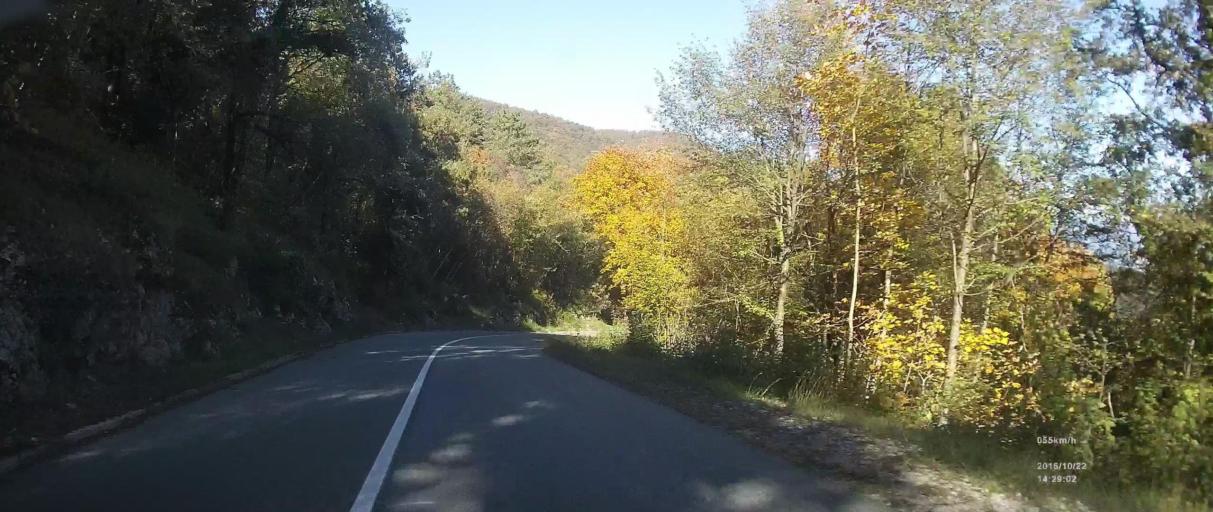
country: HR
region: Istarska
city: Lovran
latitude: 45.3289
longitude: 14.2482
